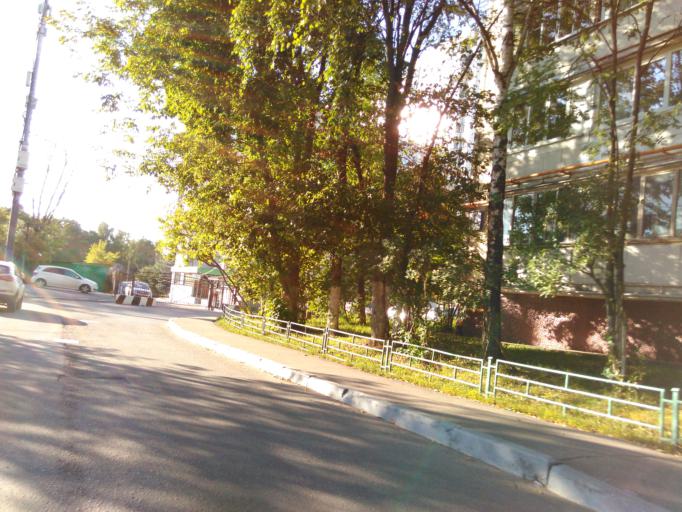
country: RU
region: Moscow
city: Tyoply Stan
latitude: 55.6275
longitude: 37.5058
